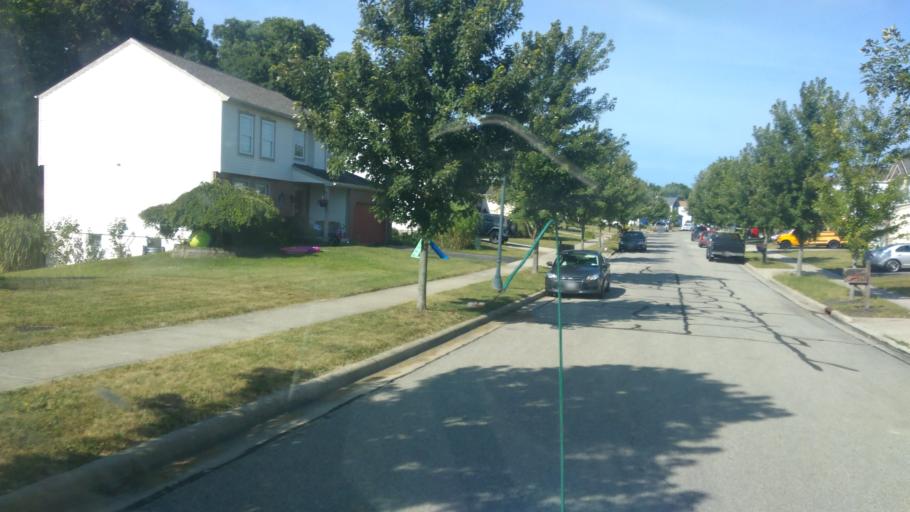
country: US
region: Ohio
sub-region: Delaware County
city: Delaware
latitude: 40.3235
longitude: -83.0782
